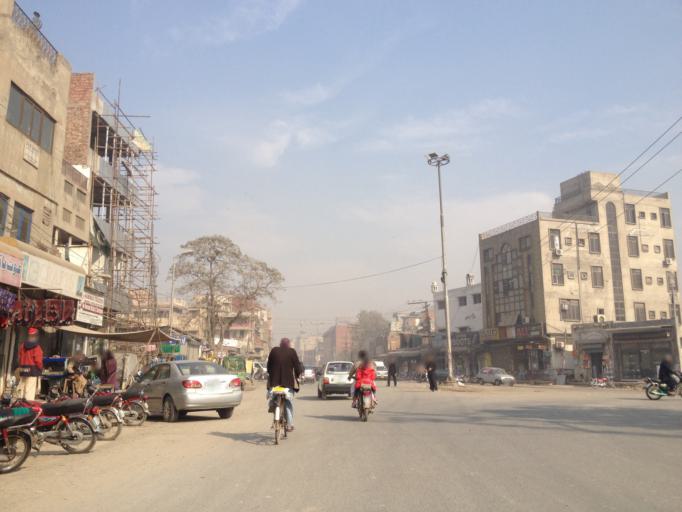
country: PK
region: Punjab
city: Lahore
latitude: 31.5619
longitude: 74.3082
